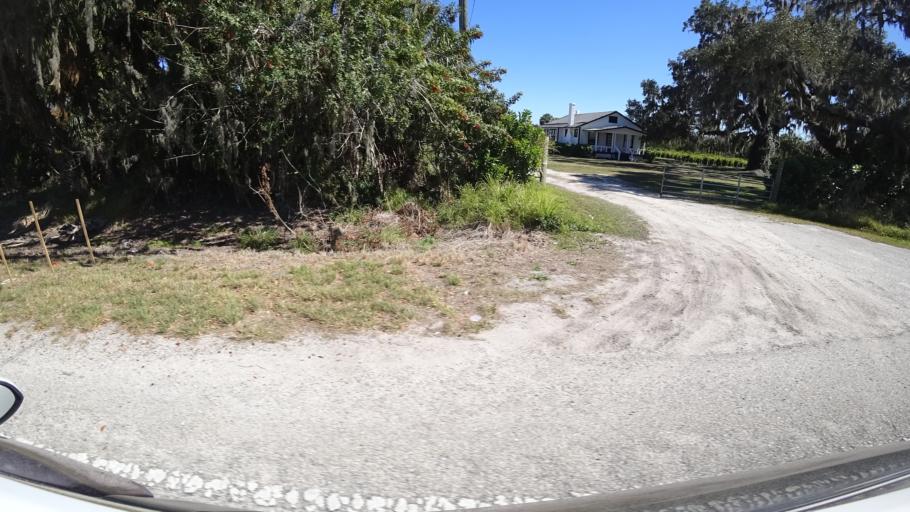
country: US
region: Florida
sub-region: Manatee County
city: Memphis
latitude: 27.5446
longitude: -82.5483
